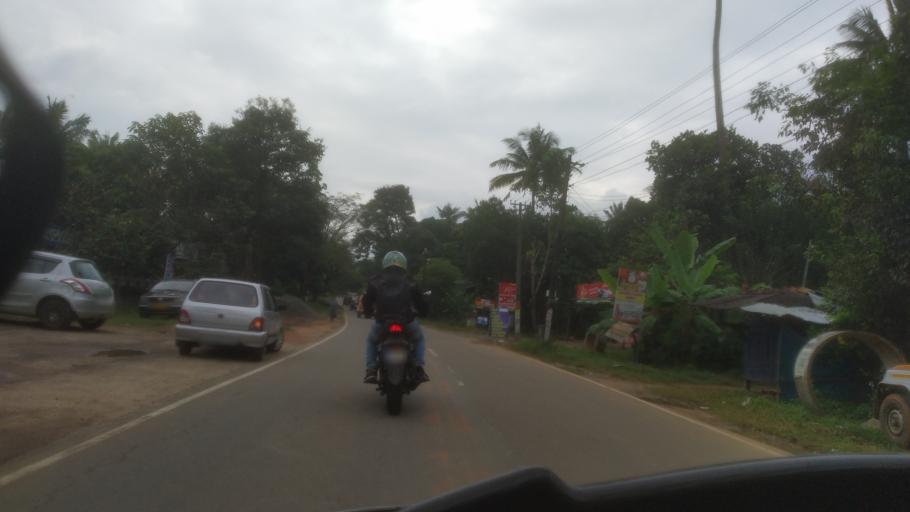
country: IN
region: Kerala
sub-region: Idukki
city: Munnar
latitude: 9.9942
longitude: 76.9773
